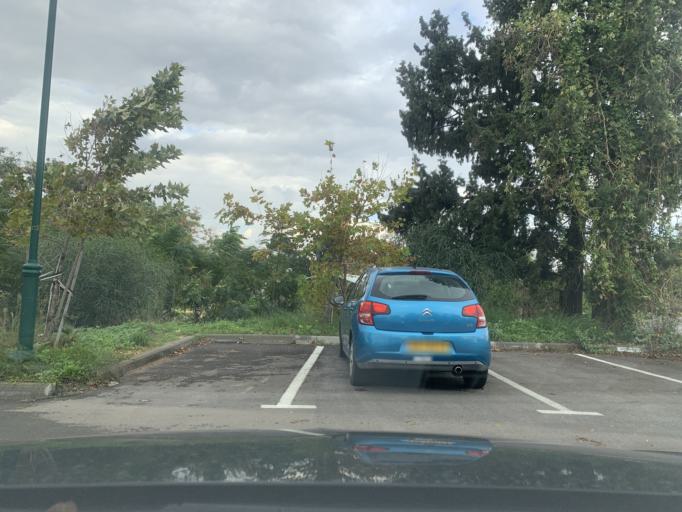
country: PS
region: West Bank
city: Qalqilyah
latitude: 32.2109
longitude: 34.9820
